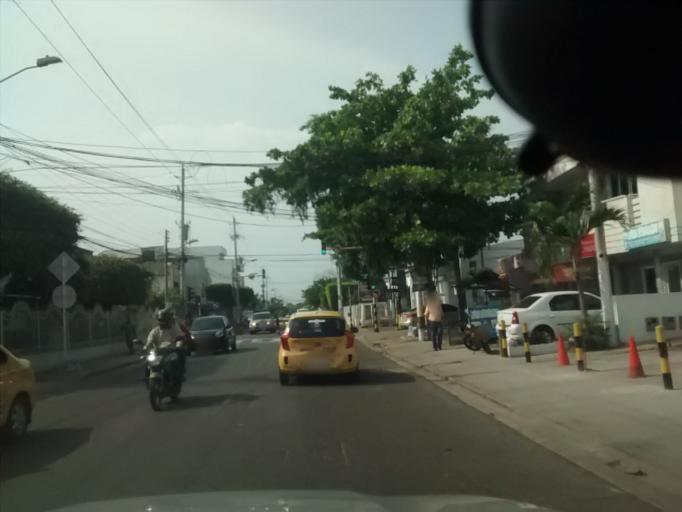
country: CO
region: Bolivar
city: Cartagena
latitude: 10.4440
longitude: -75.5178
